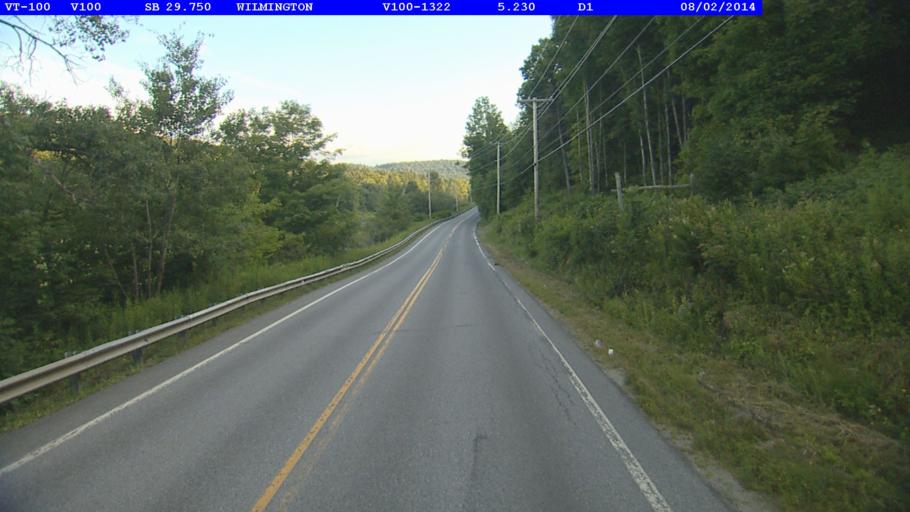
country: US
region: Vermont
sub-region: Windham County
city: Dover
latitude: 42.9016
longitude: -72.8540
